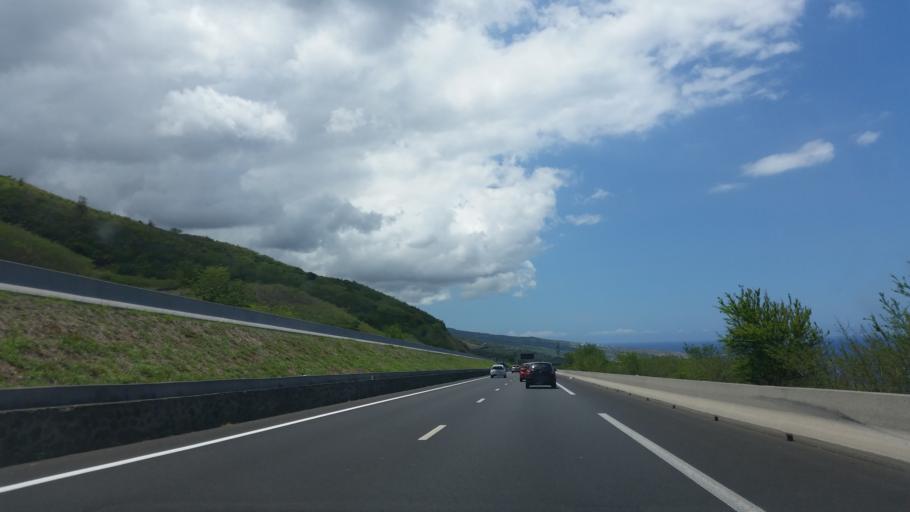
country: RE
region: Reunion
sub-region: Reunion
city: Trois-Bassins
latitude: -21.1113
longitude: 55.2749
